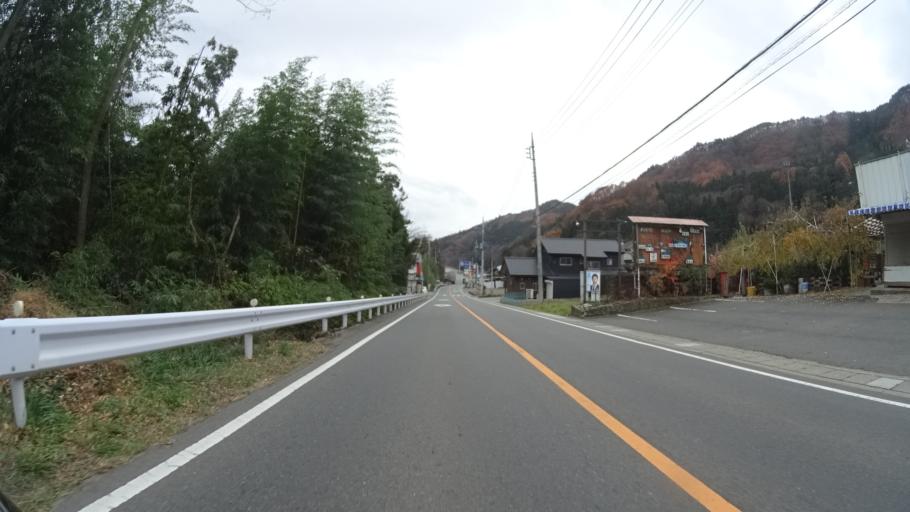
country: JP
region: Gunma
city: Numata
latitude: 36.6940
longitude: 139.2095
